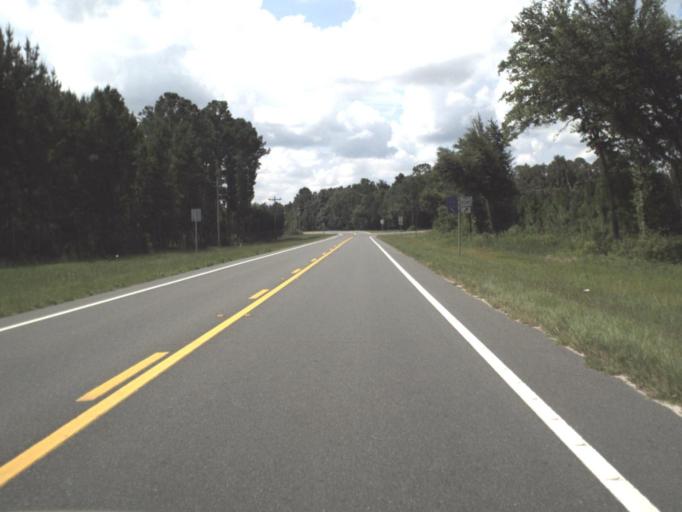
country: US
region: Florida
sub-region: Alachua County
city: Alachua
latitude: 29.8439
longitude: -82.3472
